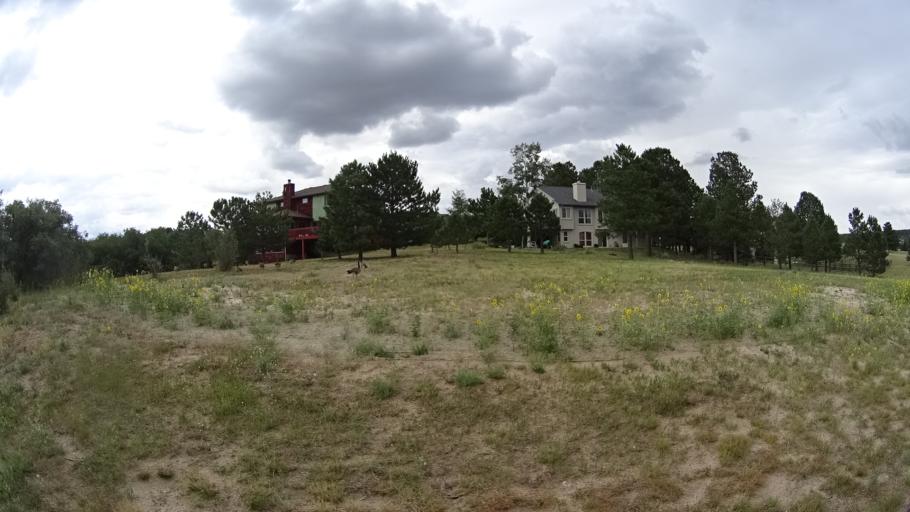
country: US
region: Colorado
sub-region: El Paso County
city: Woodmoor
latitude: 39.0986
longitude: -104.8537
